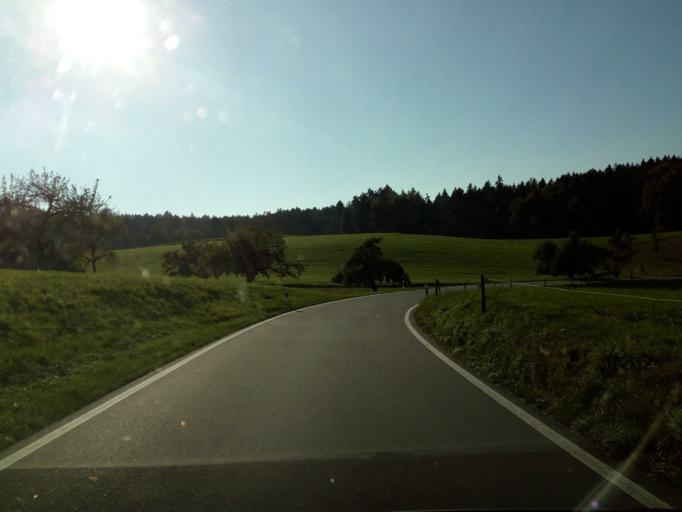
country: CH
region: Bern
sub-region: Seeland District
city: Schupfen
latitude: 47.0243
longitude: 7.3726
